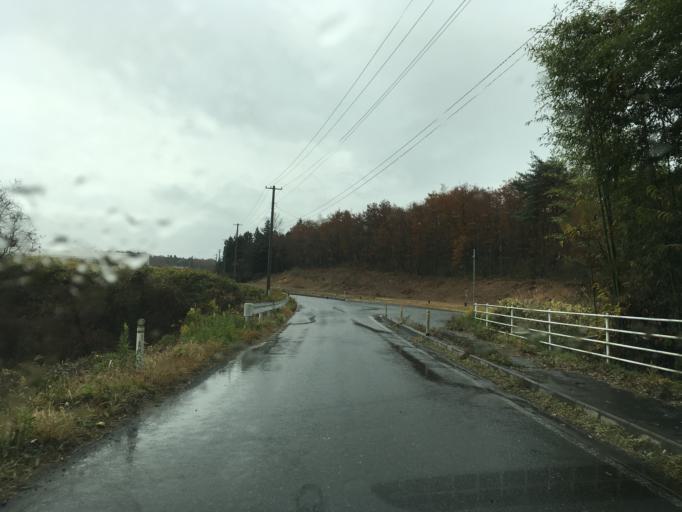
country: JP
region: Iwate
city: Ichinoseki
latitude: 38.7865
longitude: 141.2320
